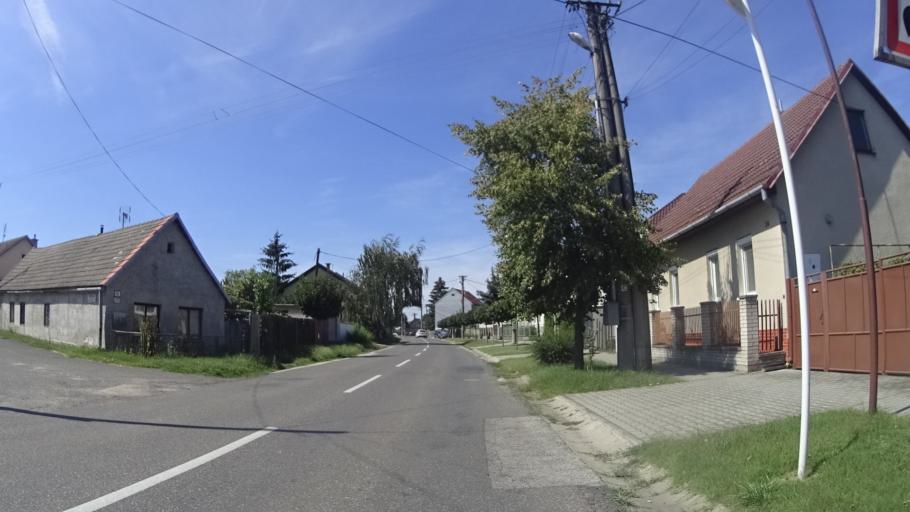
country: AT
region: Lower Austria
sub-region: Politischer Bezirk Ganserndorf
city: Marchegg
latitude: 48.3243
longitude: 16.9116
